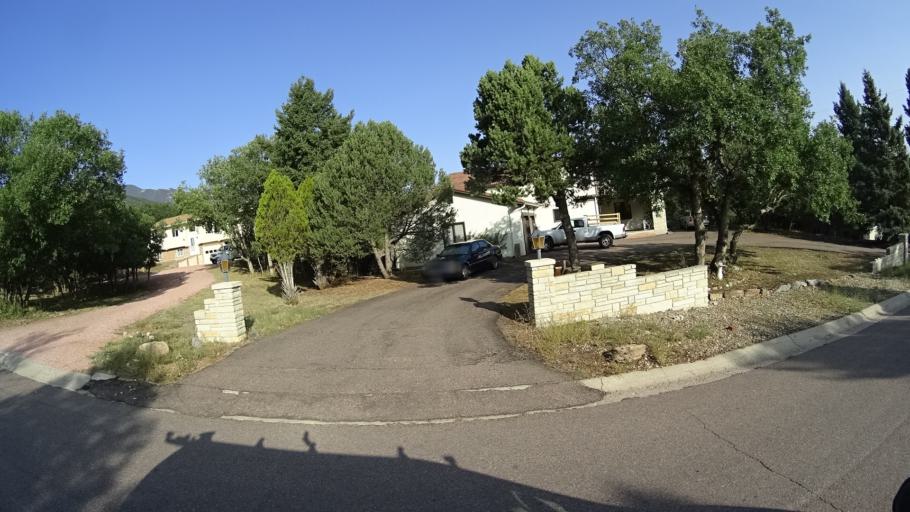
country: US
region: Colorado
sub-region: El Paso County
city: Colorado Springs
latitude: 38.8137
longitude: -104.8634
